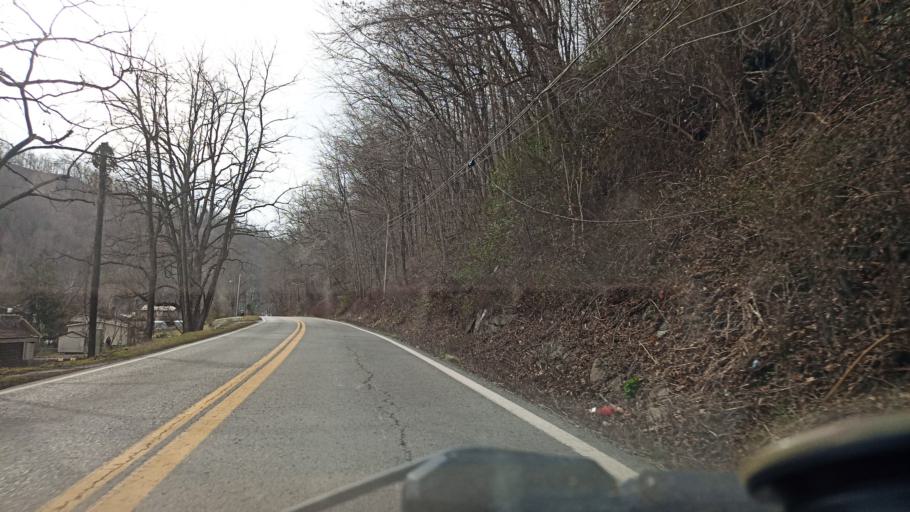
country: US
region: West Virginia
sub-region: Mingo County
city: Gilbert Creek
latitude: 37.6483
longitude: -81.8602
